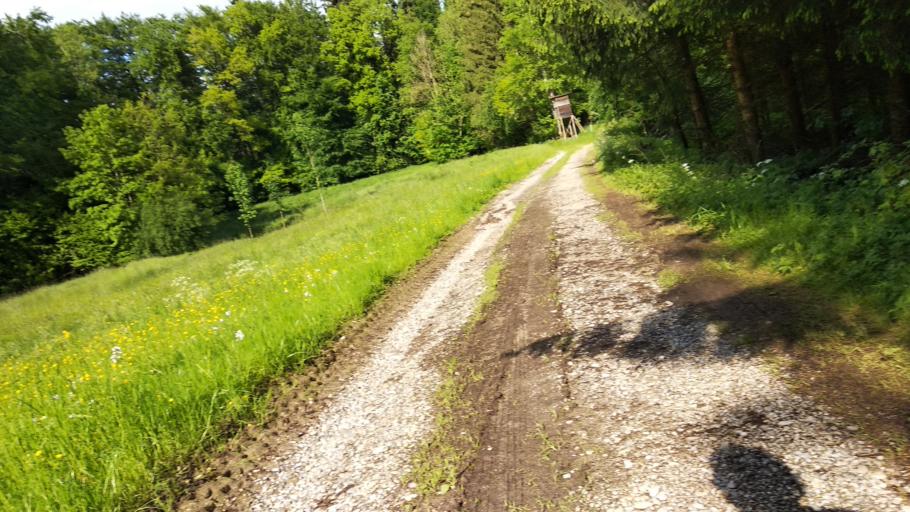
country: DE
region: Bavaria
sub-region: Swabia
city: Kronburg
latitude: 47.8837
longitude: 10.1507
